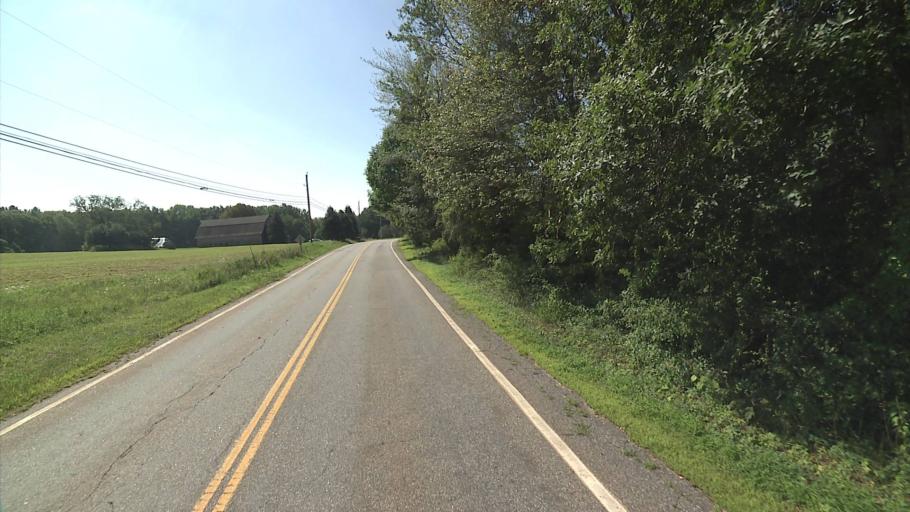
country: US
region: Connecticut
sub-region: Tolland County
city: Stafford Springs
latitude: 41.9239
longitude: -72.1922
